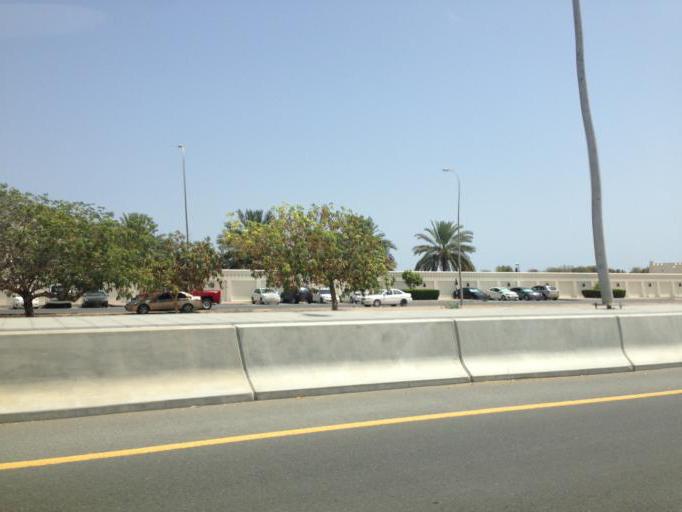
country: OM
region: Muhafazat Masqat
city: Bawshar
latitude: 23.6041
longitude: 58.3302
